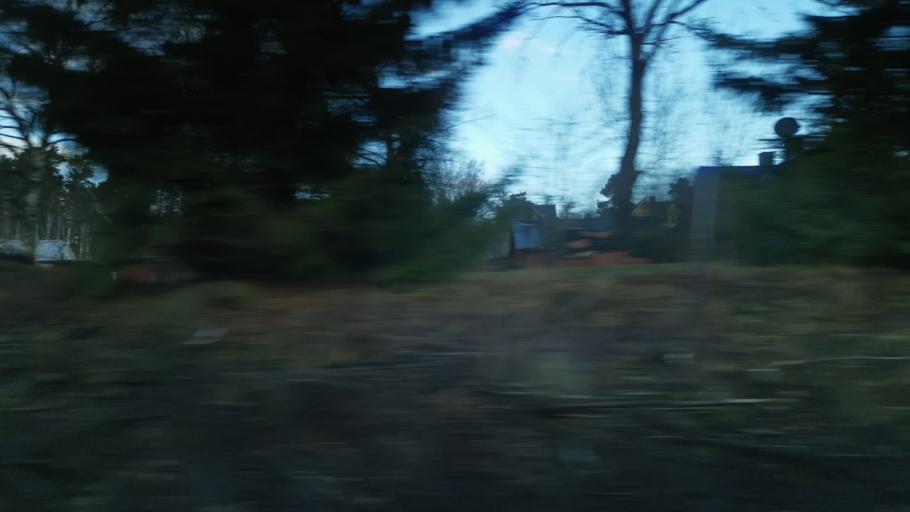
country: SE
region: Soedermanland
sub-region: Flens Kommun
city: Malmkoping
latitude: 59.0632
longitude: 16.7095
